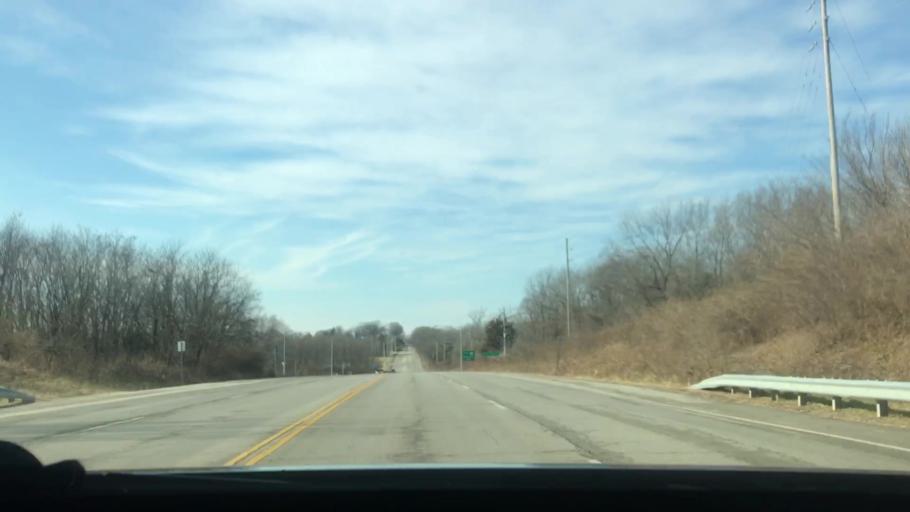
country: US
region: Missouri
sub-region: Clay County
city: Smithville
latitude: 39.3039
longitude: -94.5850
